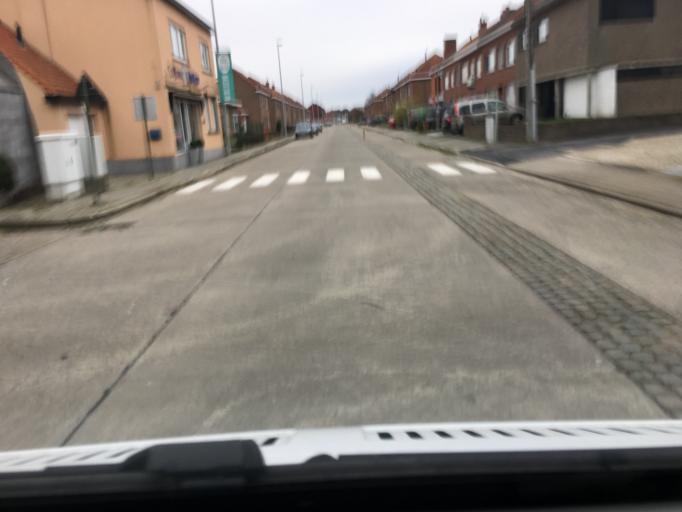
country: FR
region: Nord-Pas-de-Calais
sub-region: Departement du Nord
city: Bousbecque
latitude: 50.7818
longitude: 3.0642
